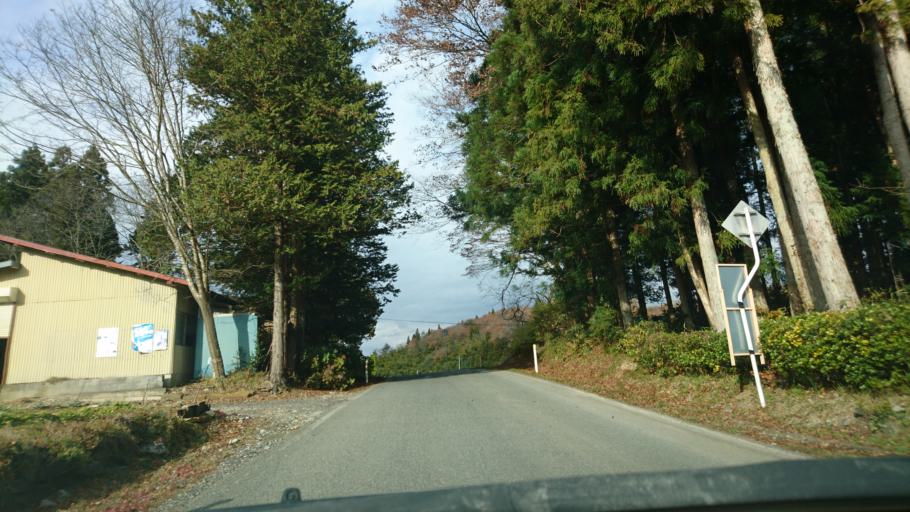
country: JP
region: Iwate
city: Ichinoseki
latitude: 39.0072
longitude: 141.2383
